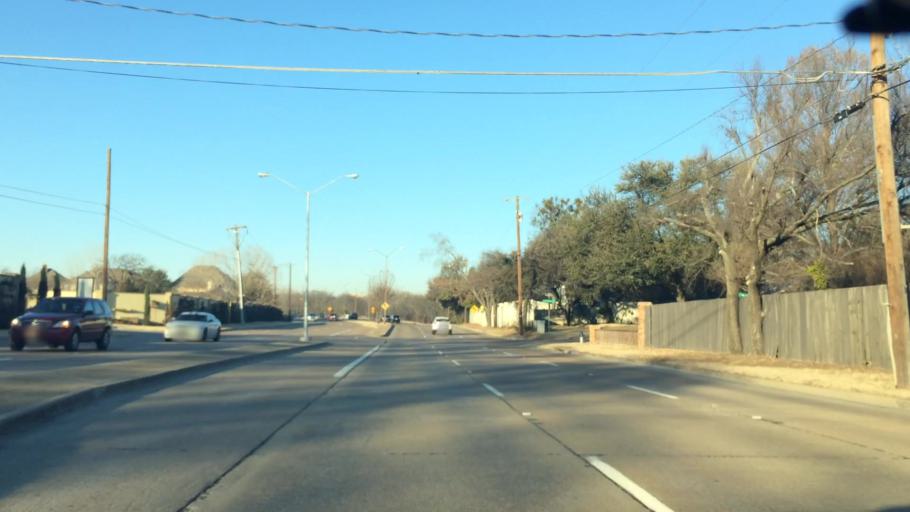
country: US
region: Texas
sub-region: Dallas County
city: Addison
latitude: 32.9400
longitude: -96.7924
